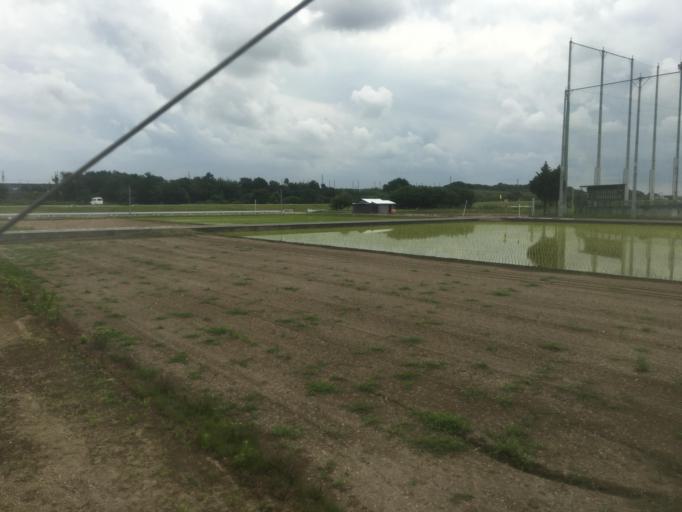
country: JP
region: Gunma
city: Takasaki
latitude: 36.2977
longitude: 139.0146
